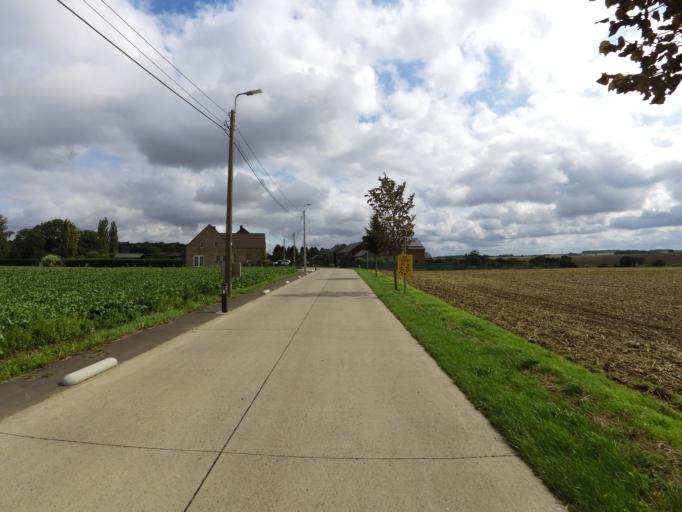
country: BE
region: Wallonia
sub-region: Province de Liege
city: Geer
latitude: 50.6153
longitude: 5.1935
